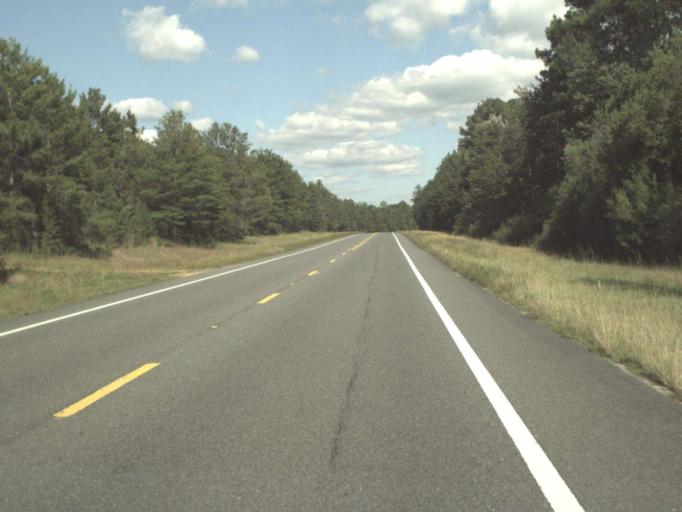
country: US
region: Florida
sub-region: Bay County
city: Laguna Beach
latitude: 30.4451
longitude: -85.8492
